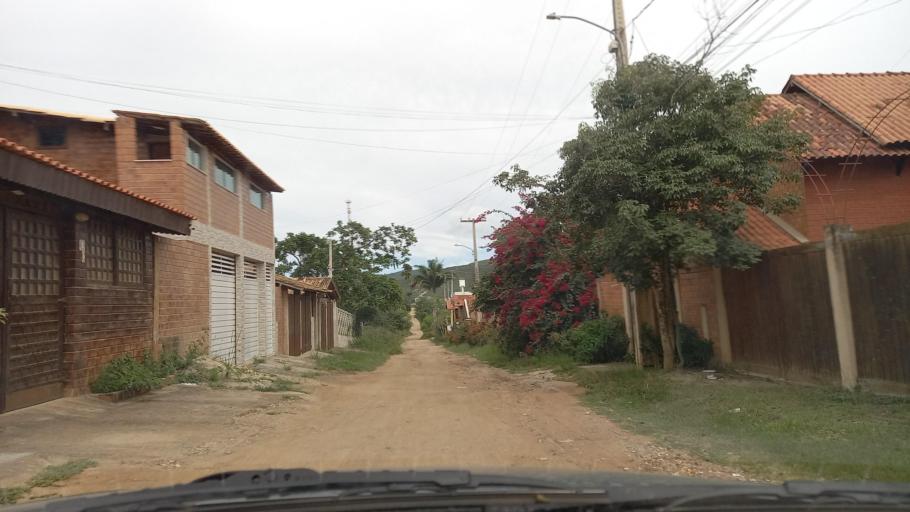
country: BR
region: Pernambuco
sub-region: Gravata
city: Gravata
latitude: -8.1974
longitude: -35.5930
